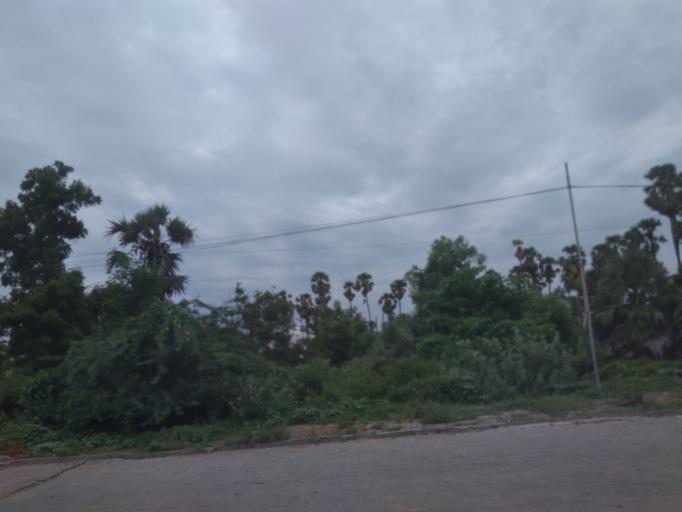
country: IN
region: Tamil Nadu
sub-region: Kancheepuram
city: Injambakkam
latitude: 12.8542
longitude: 80.2266
